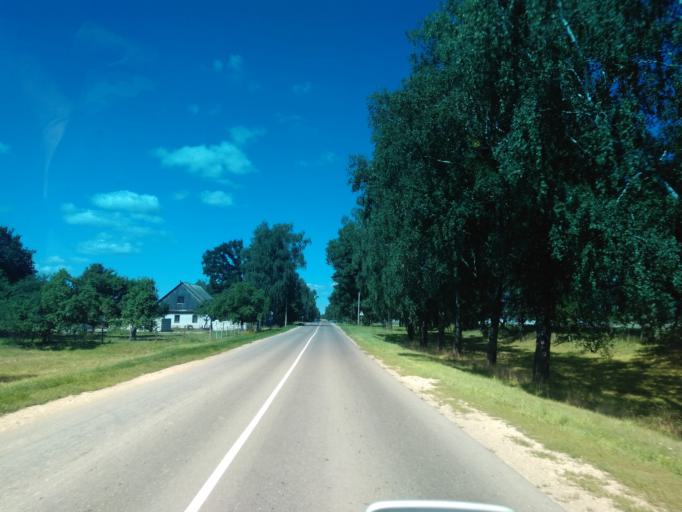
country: BY
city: Fanipol
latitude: 53.7198
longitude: 27.3404
